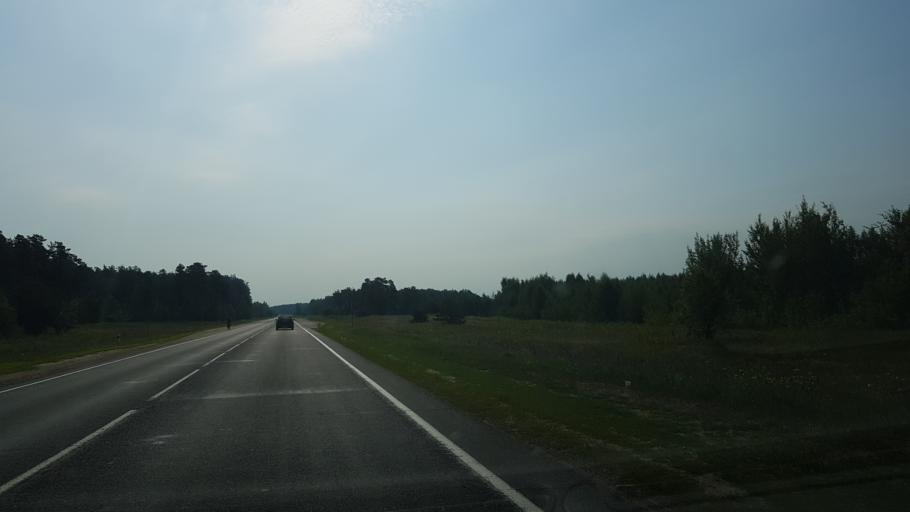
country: BY
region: Mogilev
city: Babruysk
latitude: 53.1660
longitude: 29.2862
